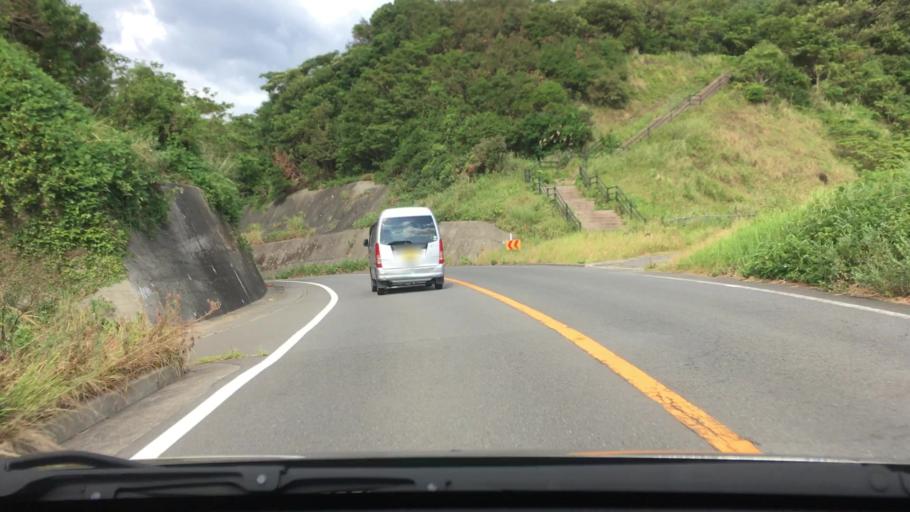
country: JP
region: Nagasaki
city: Togitsu
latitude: 32.8356
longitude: 129.7060
